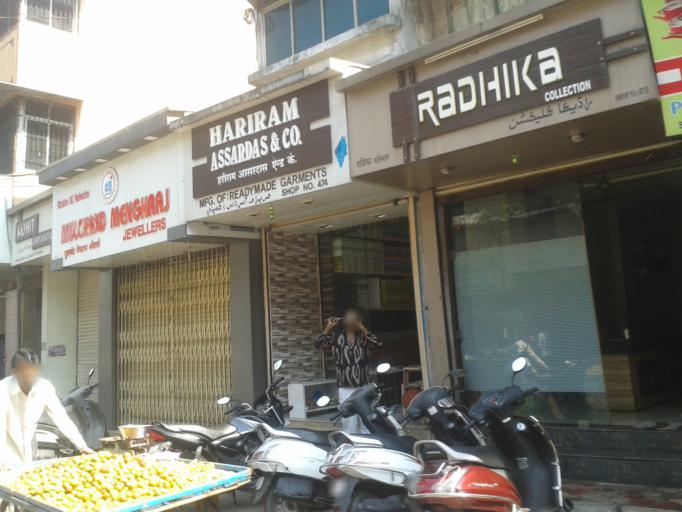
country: IN
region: Maharashtra
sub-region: Thane
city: Ulhasnagar
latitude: 19.2377
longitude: 73.1647
